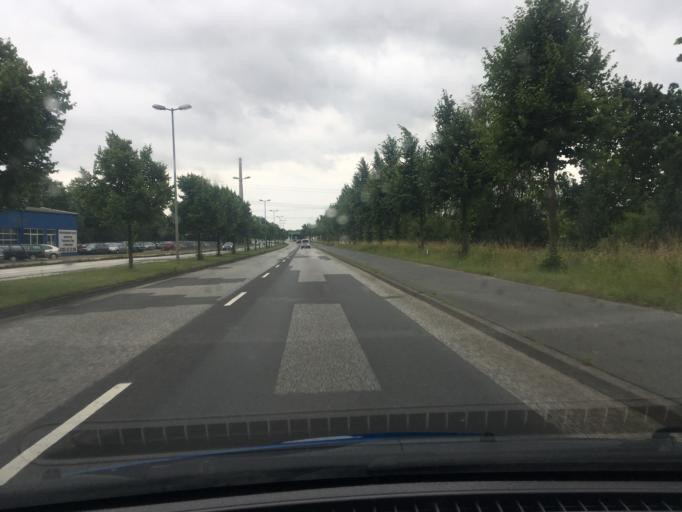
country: DE
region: Mecklenburg-Vorpommern
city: Feldstadt
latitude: 53.5891
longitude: 11.4022
